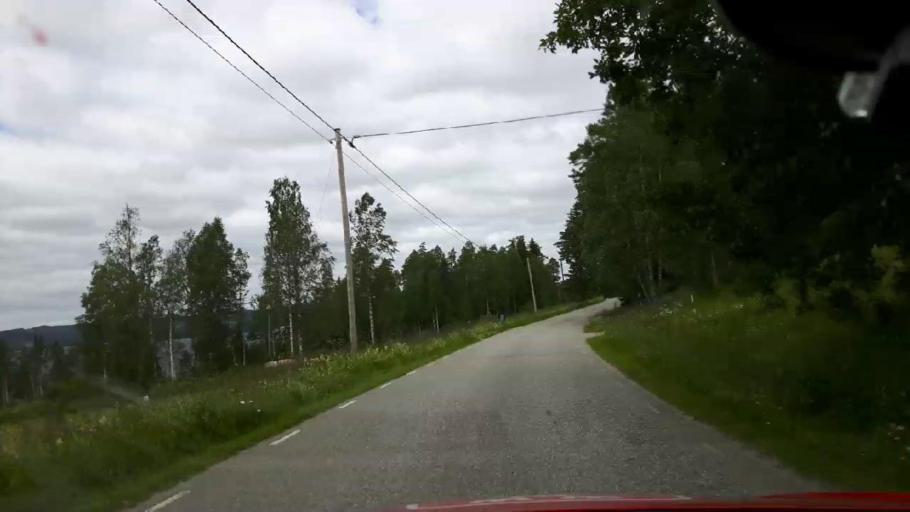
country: SE
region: Jaemtland
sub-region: Braecke Kommun
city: Braecke
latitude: 62.8816
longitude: 15.2743
